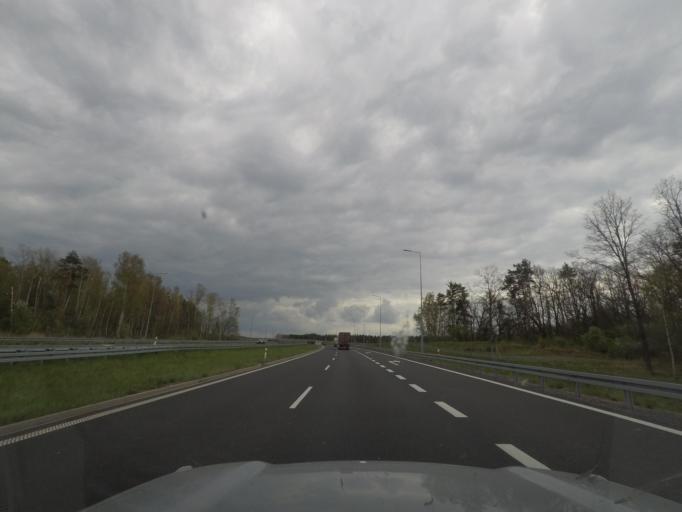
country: PL
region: Lubusz
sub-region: Powiat nowosolski
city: Nowe Miasteczko
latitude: 51.6858
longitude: 15.7571
